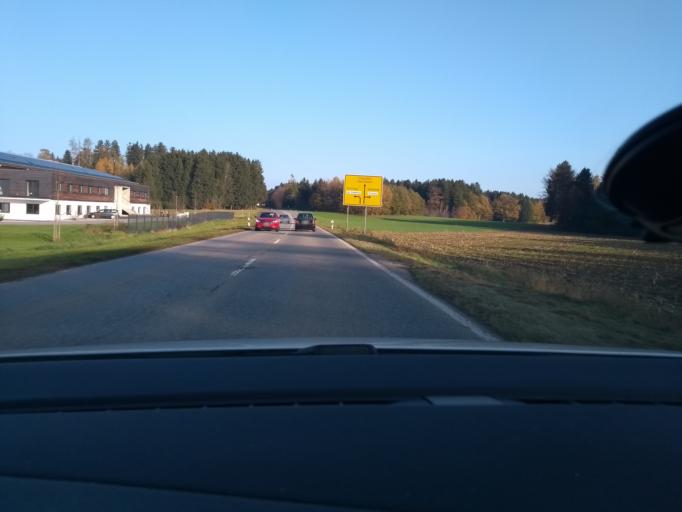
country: DE
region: Bavaria
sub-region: Upper Bavaria
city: Prutting
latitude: 47.8970
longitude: 12.2208
